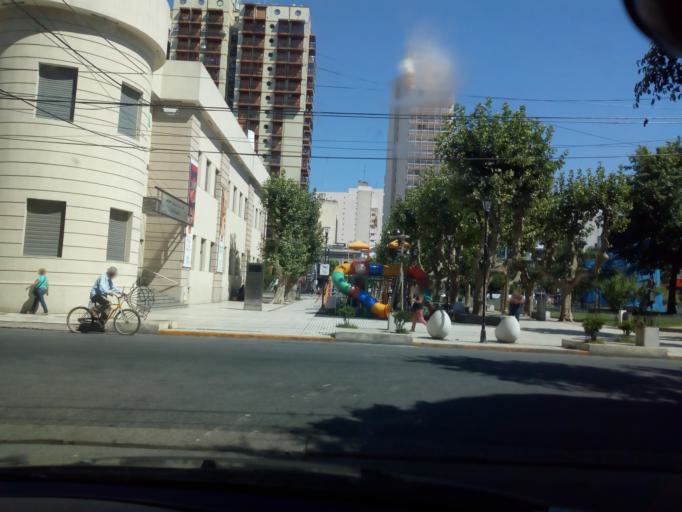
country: AR
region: Buenos Aires
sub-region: Partido de Avellaneda
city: Avellaneda
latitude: -34.6634
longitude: -58.3650
